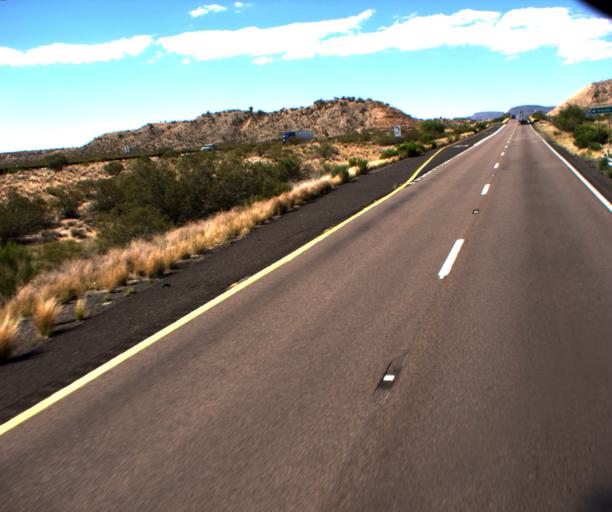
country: US
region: Arizona
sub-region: Mohave County
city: Kingman
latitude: 35.0780
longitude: -113.6653
